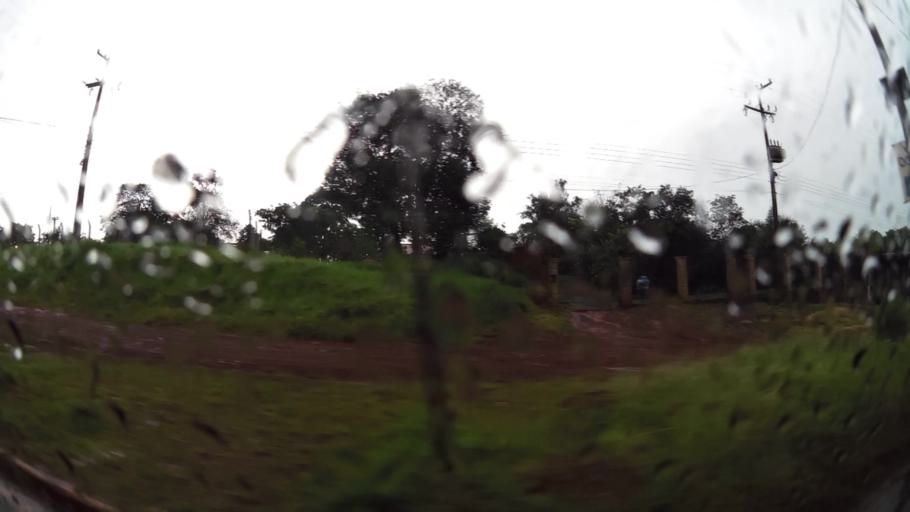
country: PY
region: Alto Parana
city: Presidente Franco
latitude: -25.5280
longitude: -54.6787
